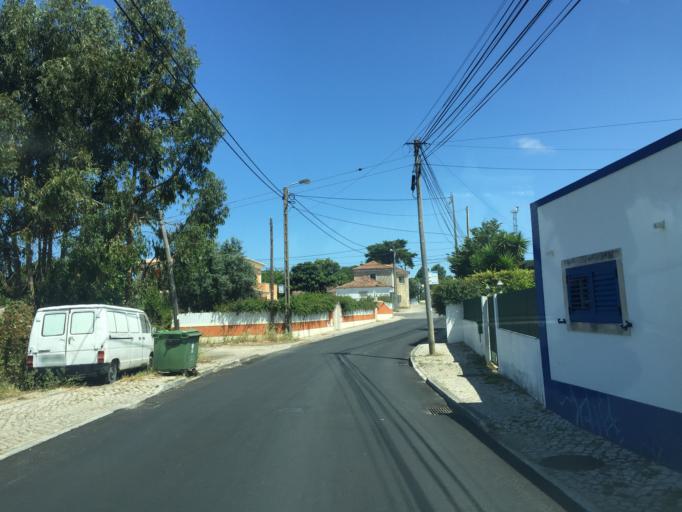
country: PT
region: Lisbon
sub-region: Sintra
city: Sintra
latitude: 38.8169
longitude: -9.4065
